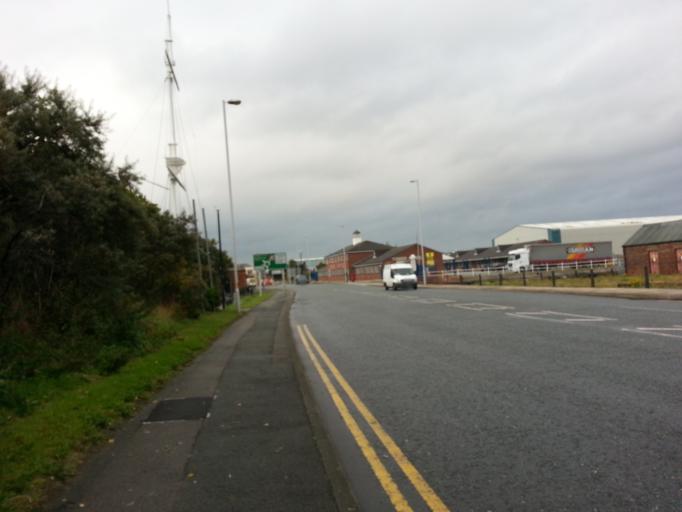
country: GB
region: England
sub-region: Metropolitan Borough of Wirral
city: Birkenhead
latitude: 53.3997
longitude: -3.0216
